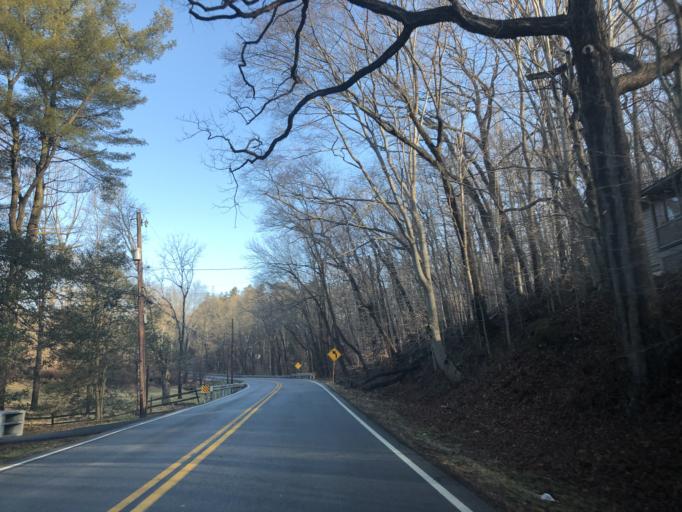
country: US
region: Pennsylvania
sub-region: Delaware County
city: Chester Heights
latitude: 39.8810
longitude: -75.4682
